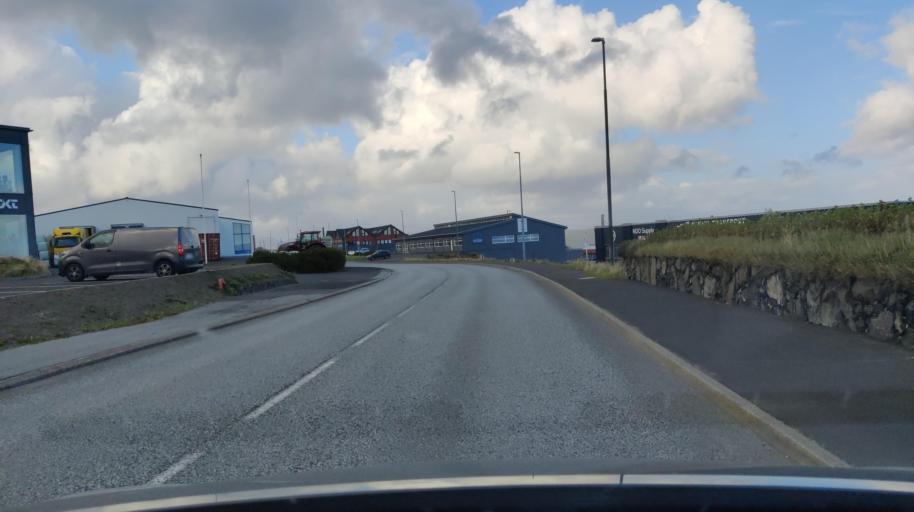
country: FO
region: Streymoy
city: Hoyvik
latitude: 62.0313
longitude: -6.7667
